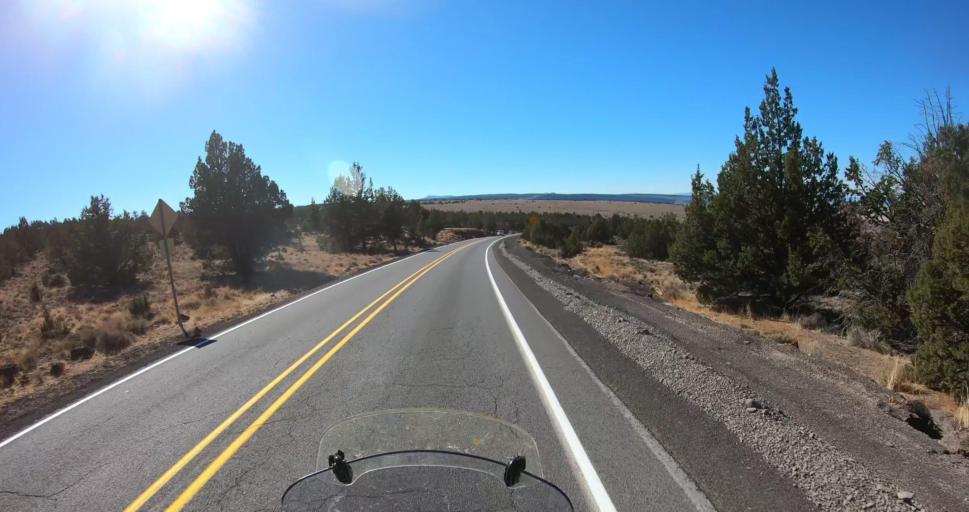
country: US
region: Oregon
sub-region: Deschutes County
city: La Pine
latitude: 43.0480
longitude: -120.8019
